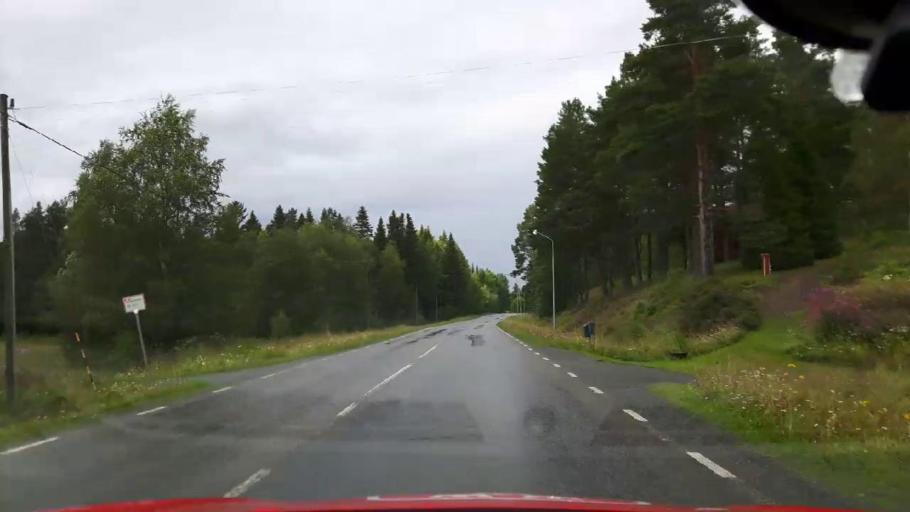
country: SE
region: Jaemtland
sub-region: Krokoms Kommun
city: Krokom
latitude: 63.3279
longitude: 14.2914
